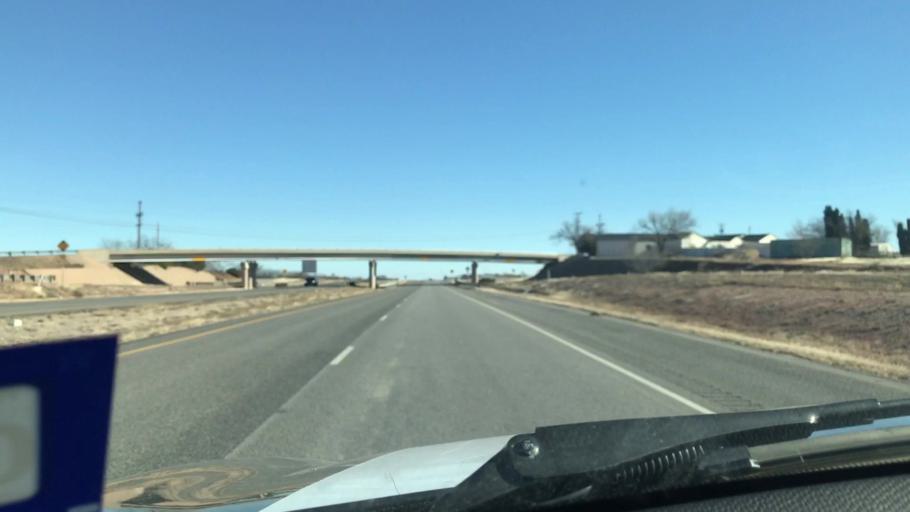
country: US
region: Texas
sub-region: Scurry County
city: Snyder
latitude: 32.7320
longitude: -100.9032
